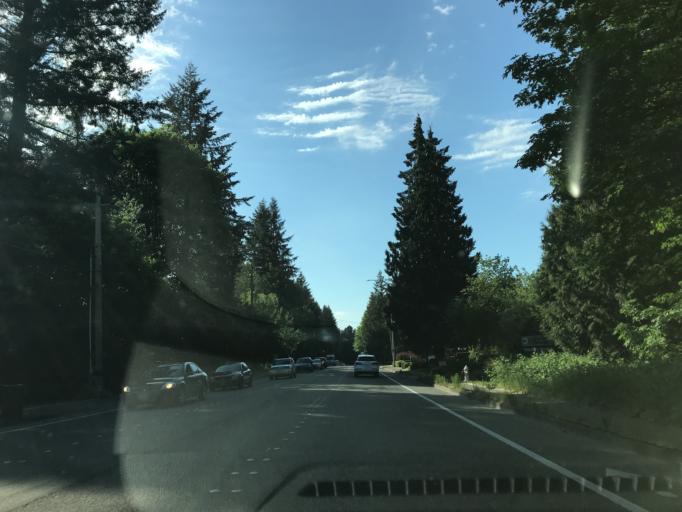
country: US
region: Washington
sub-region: King County
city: Issaquah
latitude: 47.5199
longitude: -122.0314
